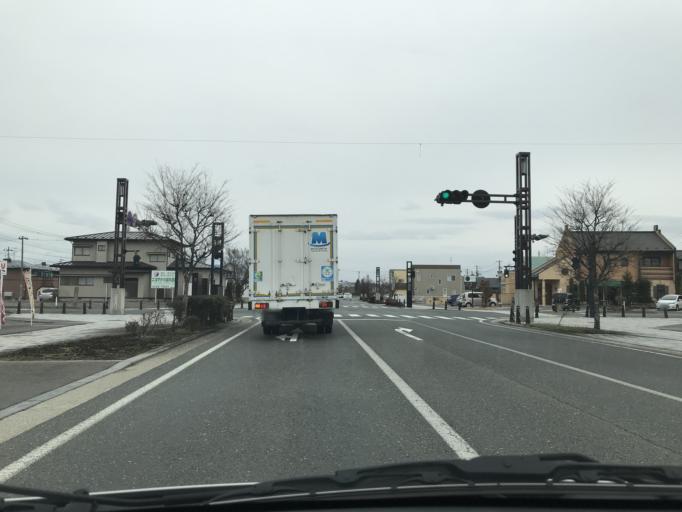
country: JP
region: Iwate
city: Hanamaki
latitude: 39.3770
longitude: 141.1118
